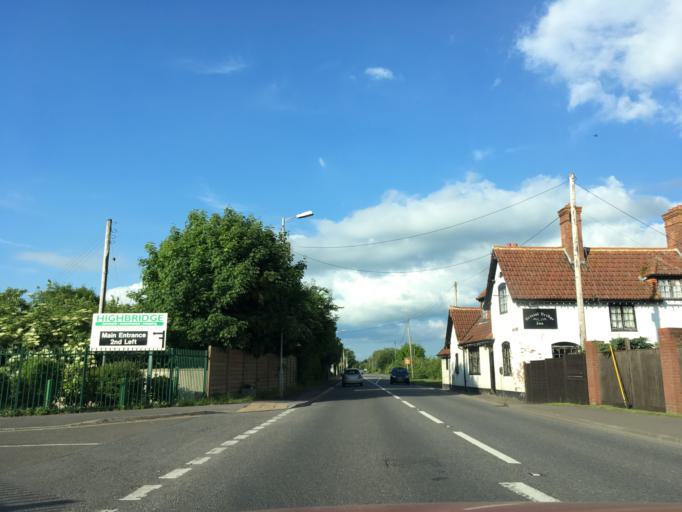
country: GB
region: England
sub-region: Somerset
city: Highbridge
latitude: 51.2258
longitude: -2.9693
